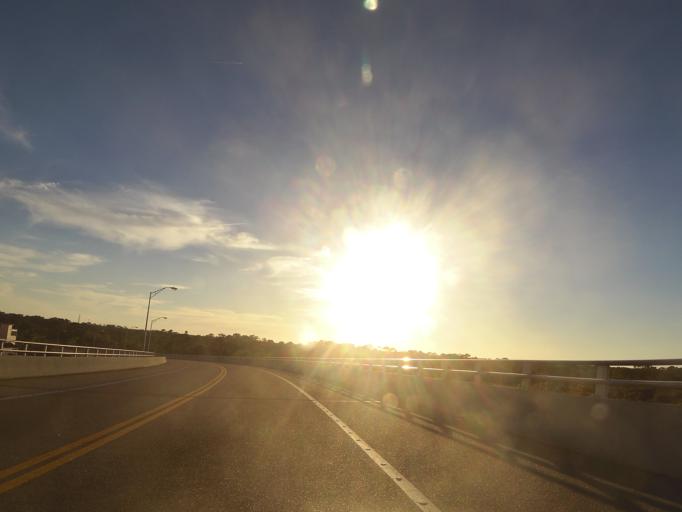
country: US
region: Florida
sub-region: Flagler County
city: Palm Coast
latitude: 29.5732
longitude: -81.1903
